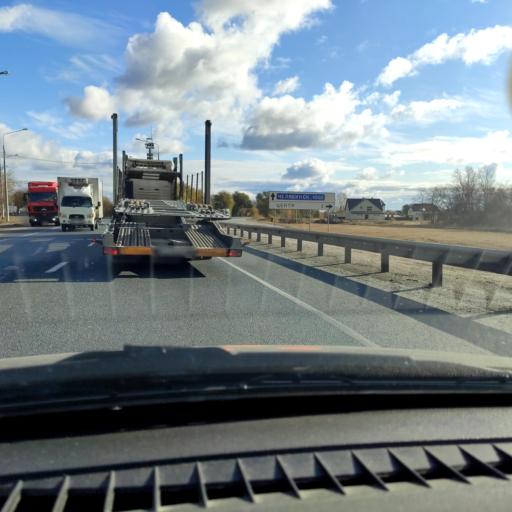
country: RU
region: Samara
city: Varlamovo
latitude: 53.1908
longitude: 48.3531
